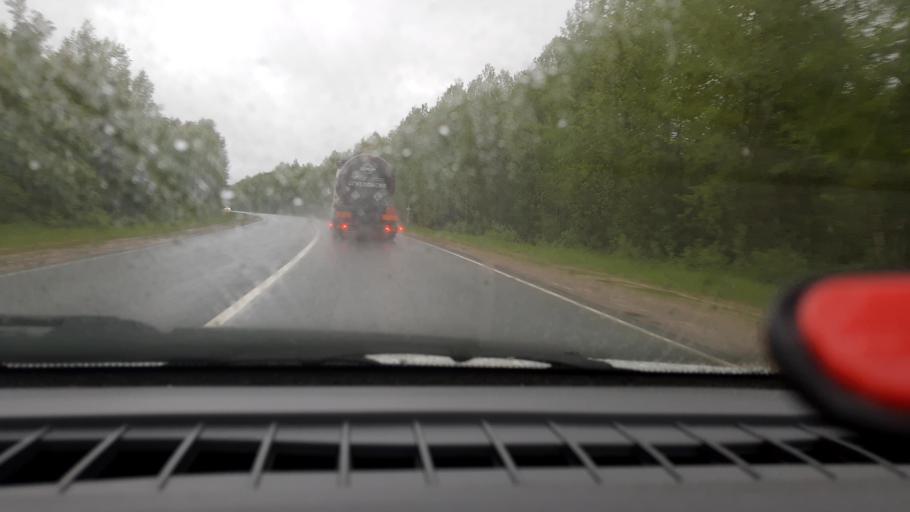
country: RU
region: Nizjnij Novgorod
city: Vladimirskoye
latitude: 56.8720
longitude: 44.9483
